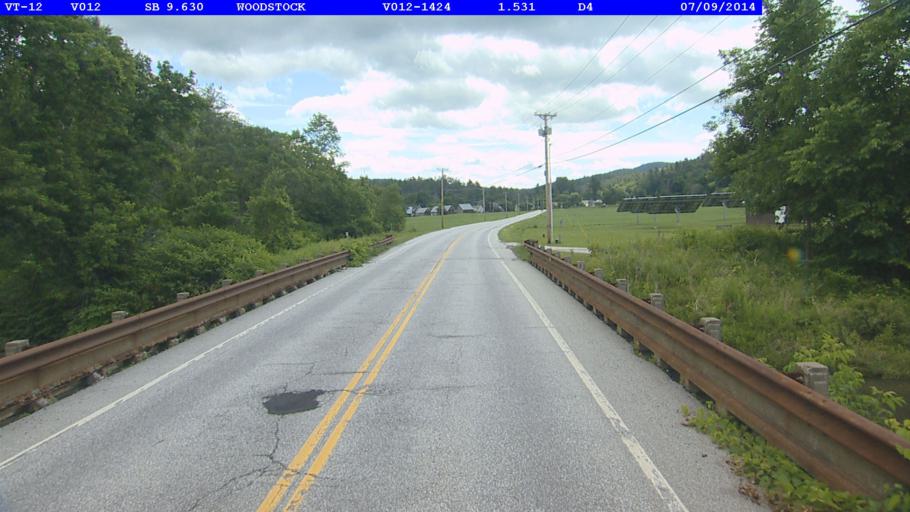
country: US
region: Vermont
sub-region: Windsor County
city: Woodstock
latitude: 43.6426
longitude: -72.5301
